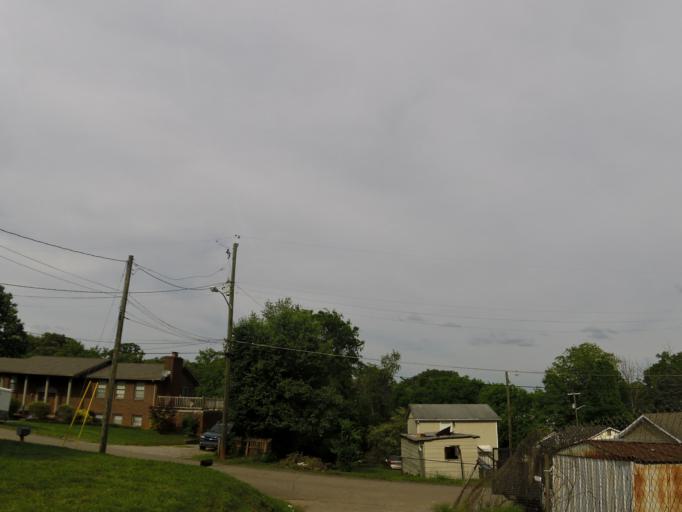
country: US
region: Tennessee
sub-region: Knox County
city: Knoxville
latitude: 35.9967
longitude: -83.9080
